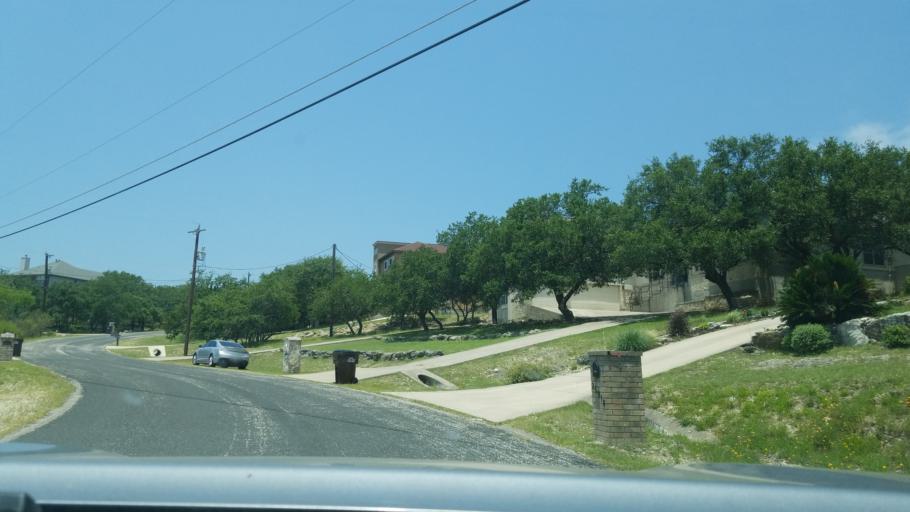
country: US
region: Texas
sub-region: Bexar County
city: Timberwood Park
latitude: 29.6865
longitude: -98.5139
